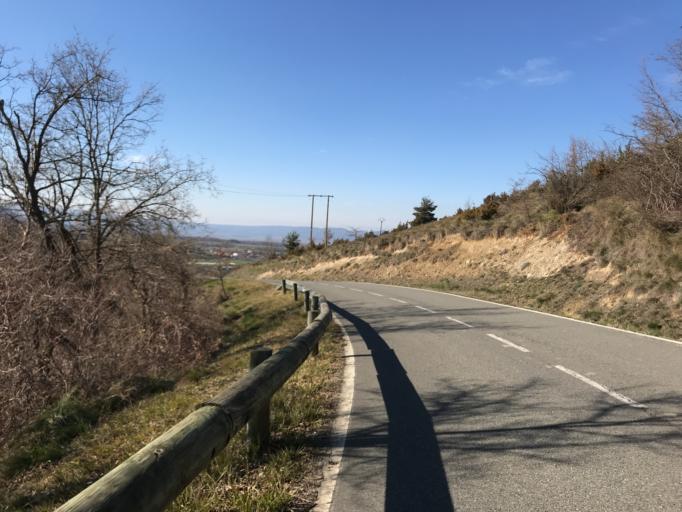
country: ES
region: Basque Country
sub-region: Provincia de Alava
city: Gasteiz / Vitoria
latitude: 42.8087
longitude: -2.6770
